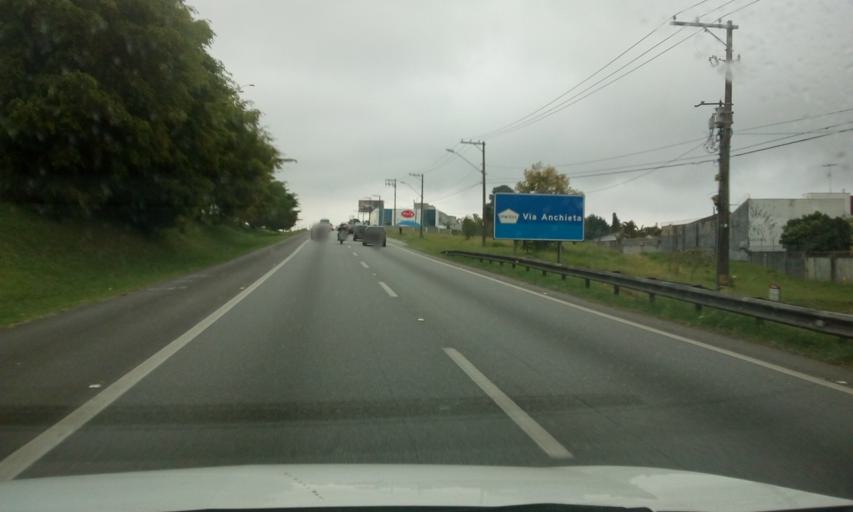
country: BR
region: Sao Paulo
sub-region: Sao Bernardo Do Campo
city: Sao Bernardo do Campo
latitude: -23.6828
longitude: -46.5669
